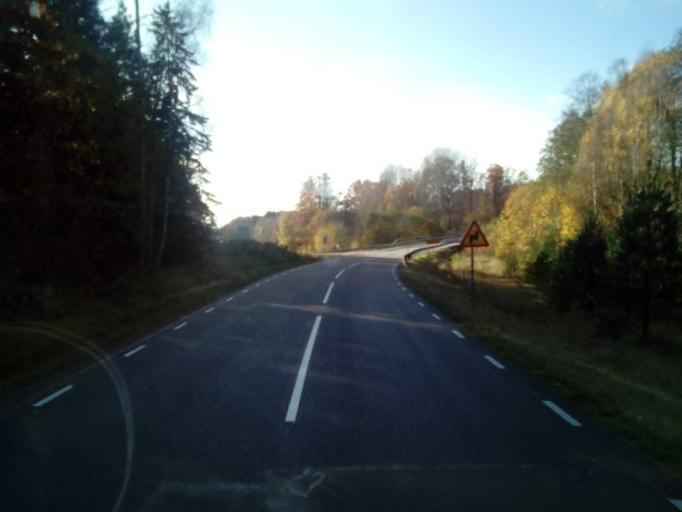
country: SE
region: Kalmar
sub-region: Vasterviks Kommun
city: Ankarsrum
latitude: 57.7338
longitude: 16.0931
